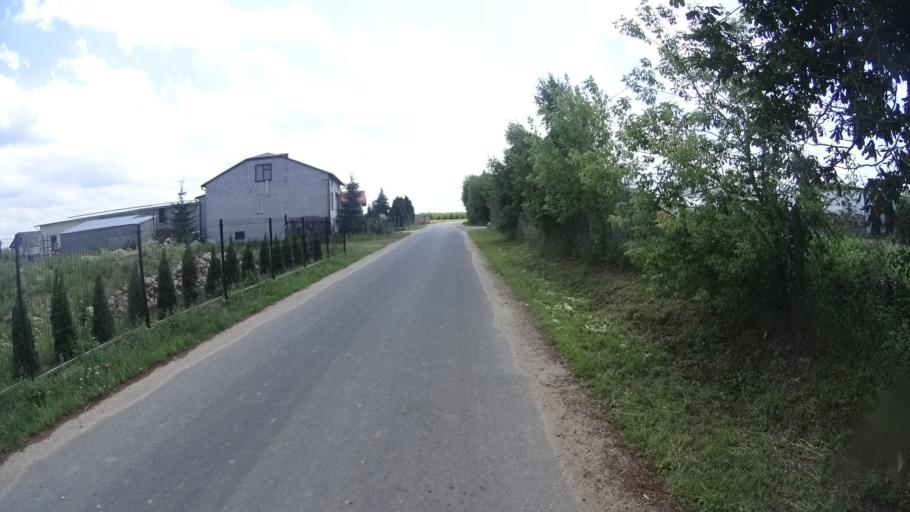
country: PL
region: Masovian Voivodeship
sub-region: Powiat grojecki
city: Goszczyn
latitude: 51.7162
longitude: 20.8340
